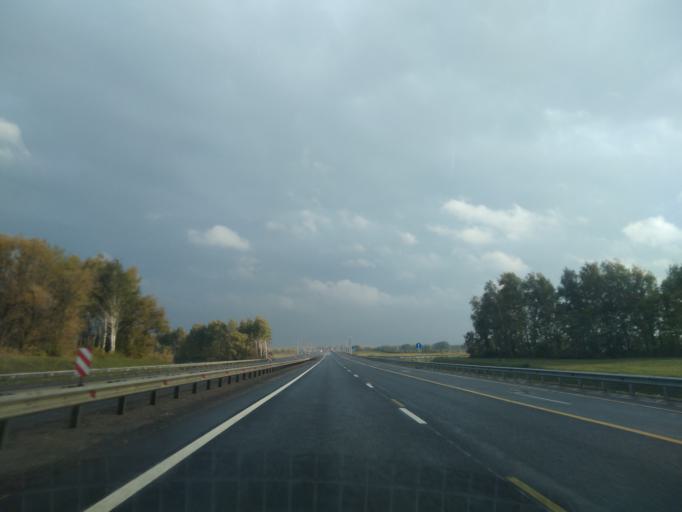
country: RU
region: Lipetsk
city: Yelets
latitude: 52.5790
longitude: 38.6913
